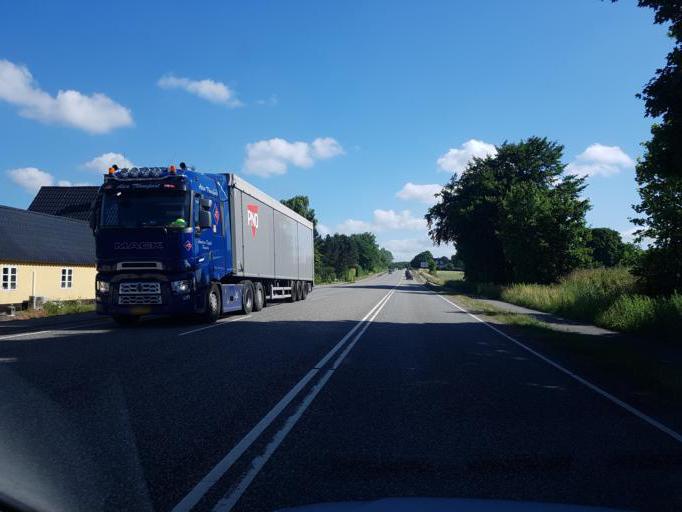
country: DK
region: Zealand
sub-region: Lejre Kommune
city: Kirke Hvalso
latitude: 55.5039
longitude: 11.8833
